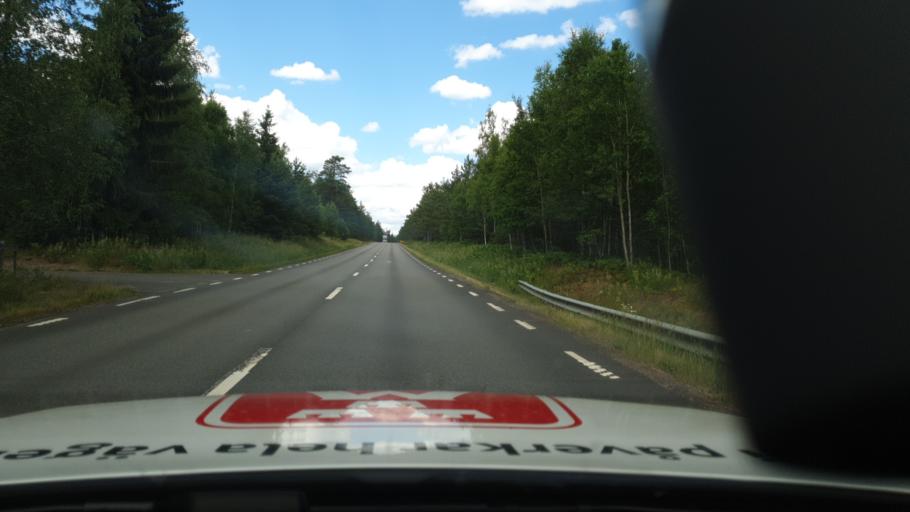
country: SE
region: Vaestra Goetaland
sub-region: Karlsborgs Kommun
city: Molltorp
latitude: 58.4720
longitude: 14.4073
